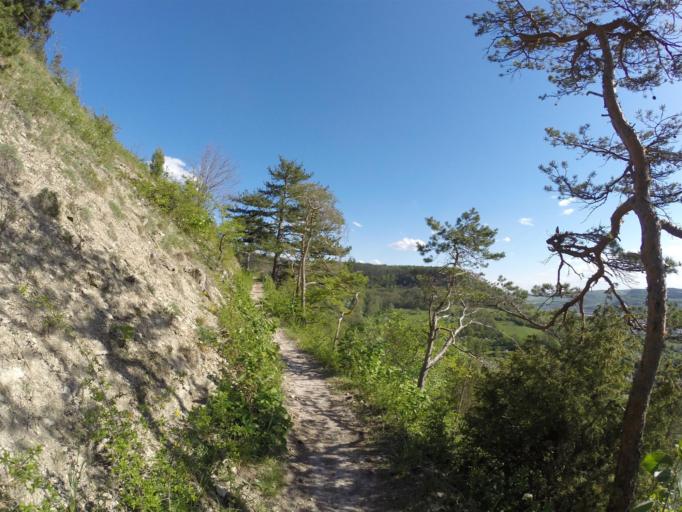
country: DE
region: Thuringia
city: Jena
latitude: 50.9097
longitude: 11.6072
